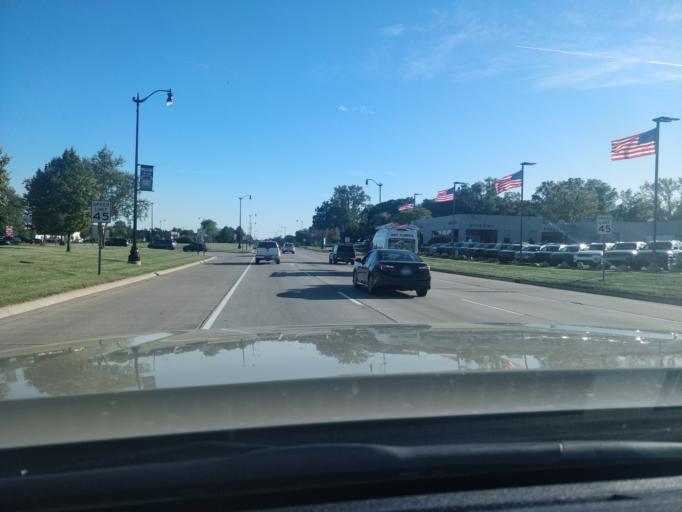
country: US
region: Michigan
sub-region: Wayne County
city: Taylor
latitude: 42.2179
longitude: -83.2690
